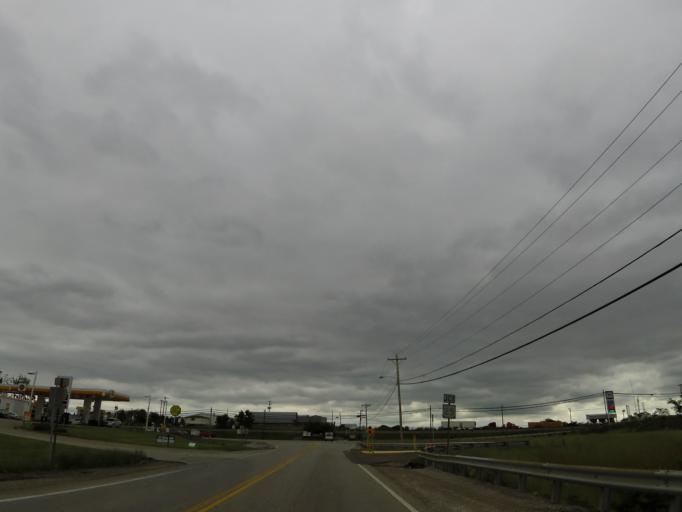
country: US
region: Kentucky
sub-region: Grant County
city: Williamstown
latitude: 38.6258
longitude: -84.5698
